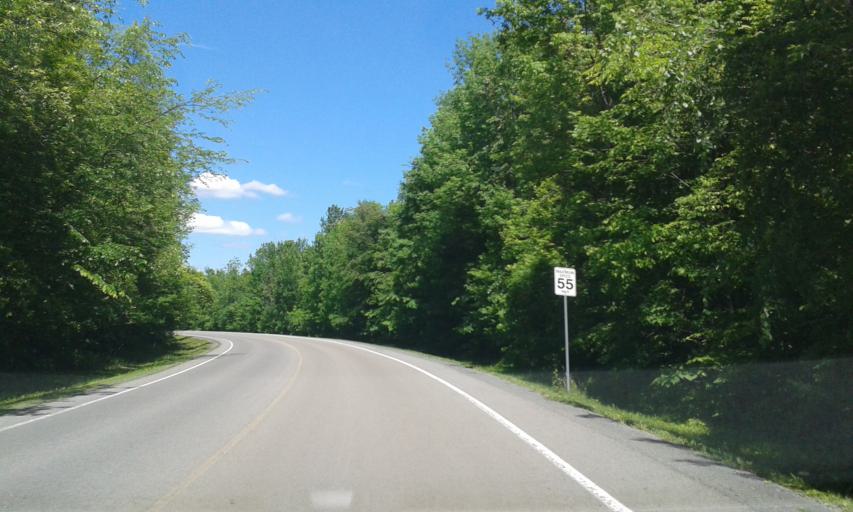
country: US
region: New York
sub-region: St. Lawrence County
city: Massena
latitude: 45.0179
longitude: -74.8932
